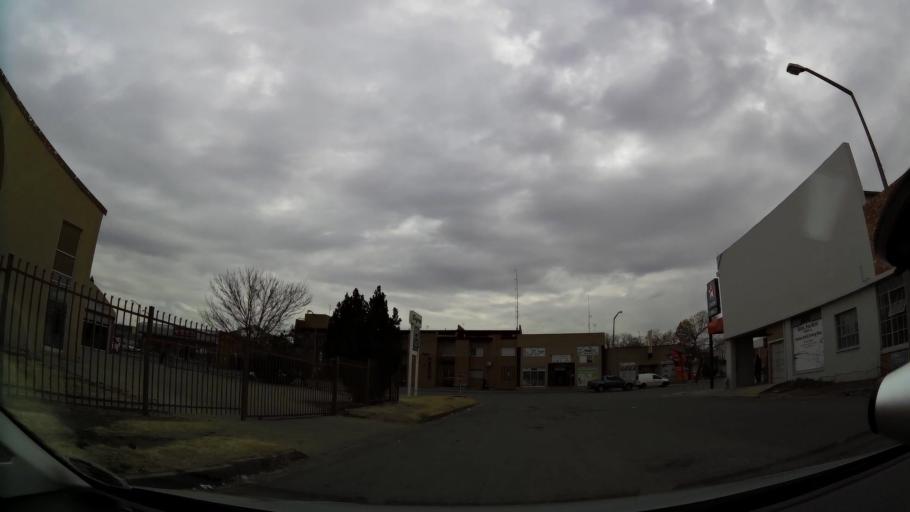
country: ZA
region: Orange Free State
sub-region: Fezile Dabi District Municipality
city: Kroonstad
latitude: -27.6613
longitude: 27.2378
